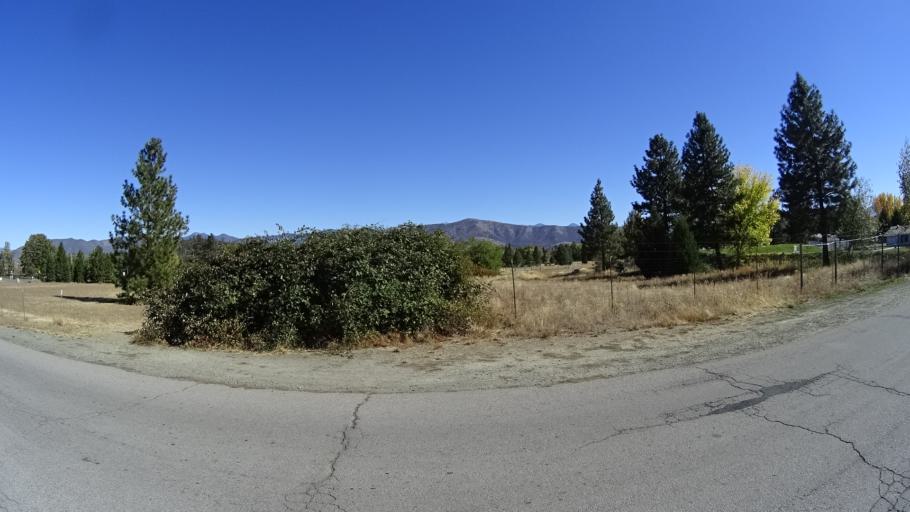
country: US
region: California
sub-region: Siskiyou County
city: Yreka
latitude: 41.4621
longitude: -122.8982
